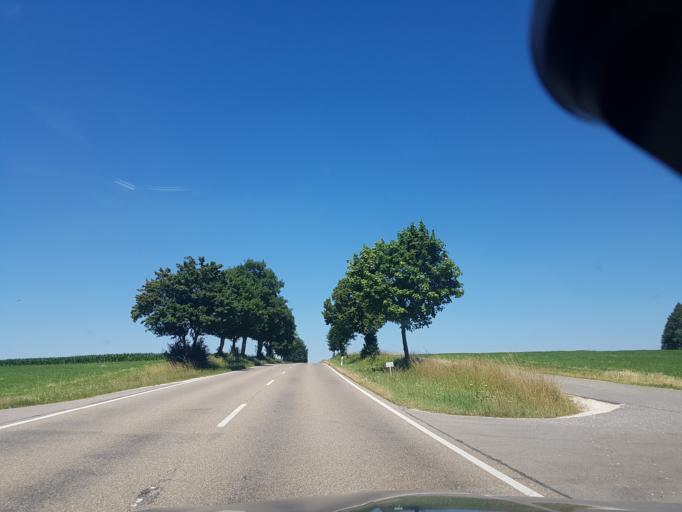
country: DE
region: Bavaria
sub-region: Swabia
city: Pfaffenhofen an der Roth
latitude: 48.3744
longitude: 10.1667
